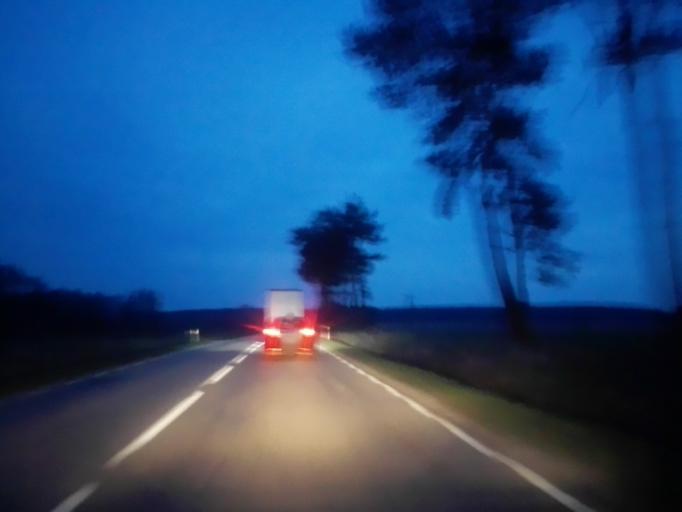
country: PL
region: Podlasie
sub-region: Powiat lomzynski
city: Sniadowo
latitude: 53.0978
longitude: 22.0248
